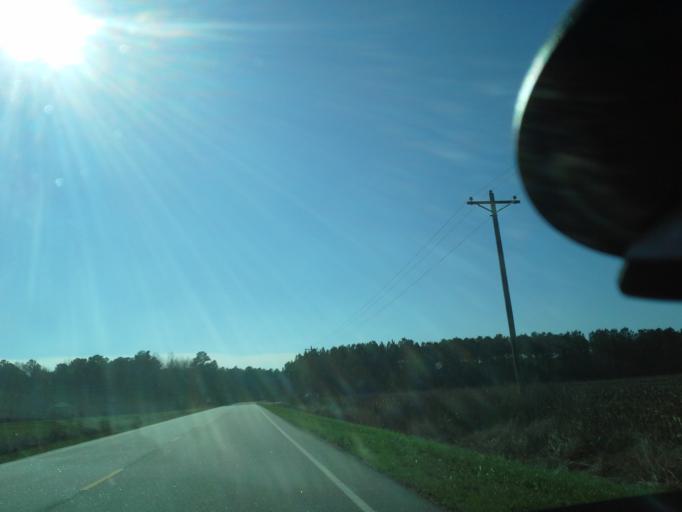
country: US
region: North Carolina
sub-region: Beaufort County
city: Belhaven
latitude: 35.5750
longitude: -76.6875
